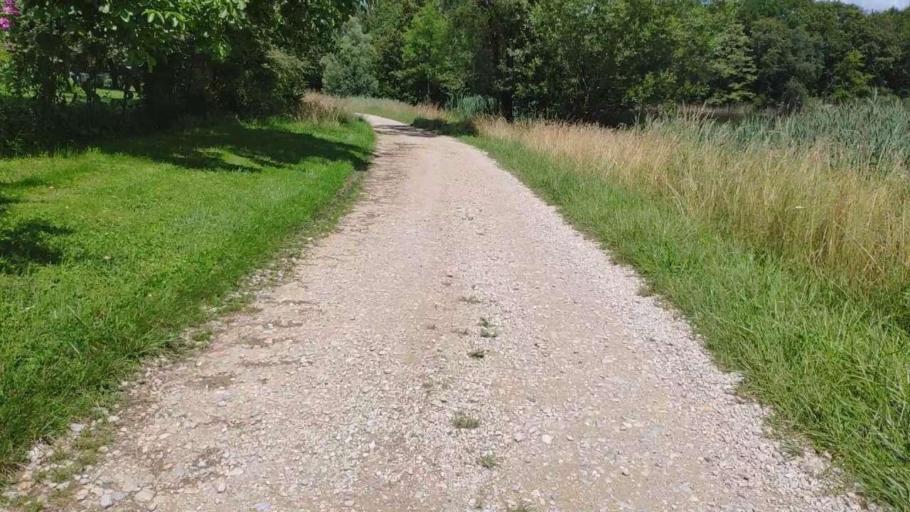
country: FR
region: Franche-Comte
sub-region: Departement du Jura
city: Chaussin
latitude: 46.8783
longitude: 5.4909
